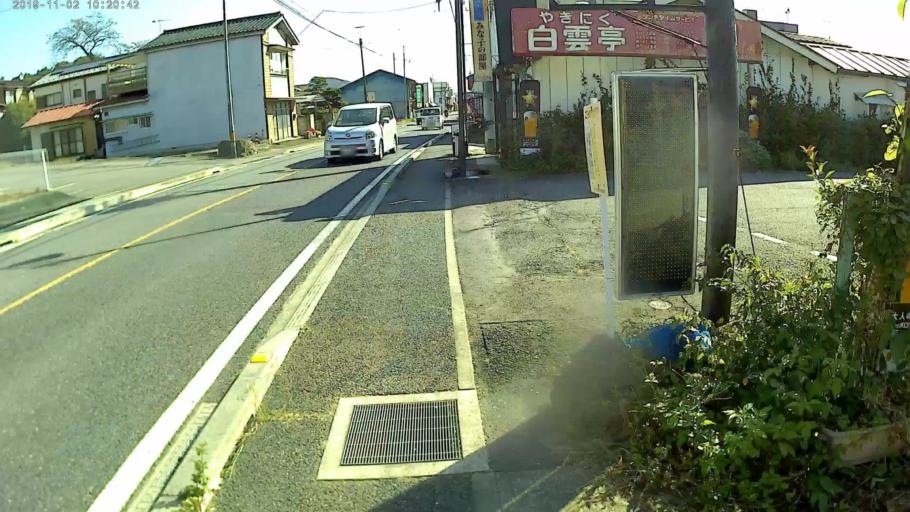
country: JP
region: Gunma
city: Annaka
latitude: 36.3144
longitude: 138.7988
